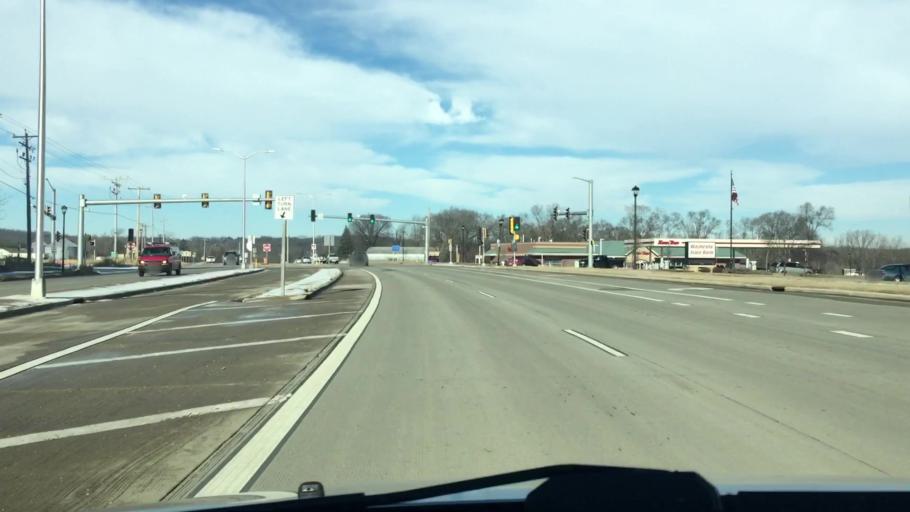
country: US
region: Wisconsin
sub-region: Waukesha County
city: Mukwonago
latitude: 42.8794
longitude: -88.3405
